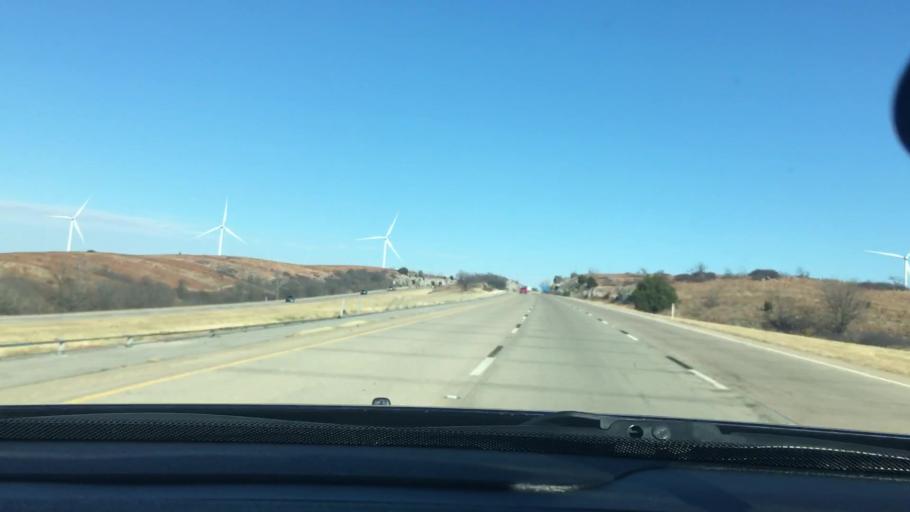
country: US
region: Oklahoma
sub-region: Murray County
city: Davis
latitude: 34.3653
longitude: -97.1466
